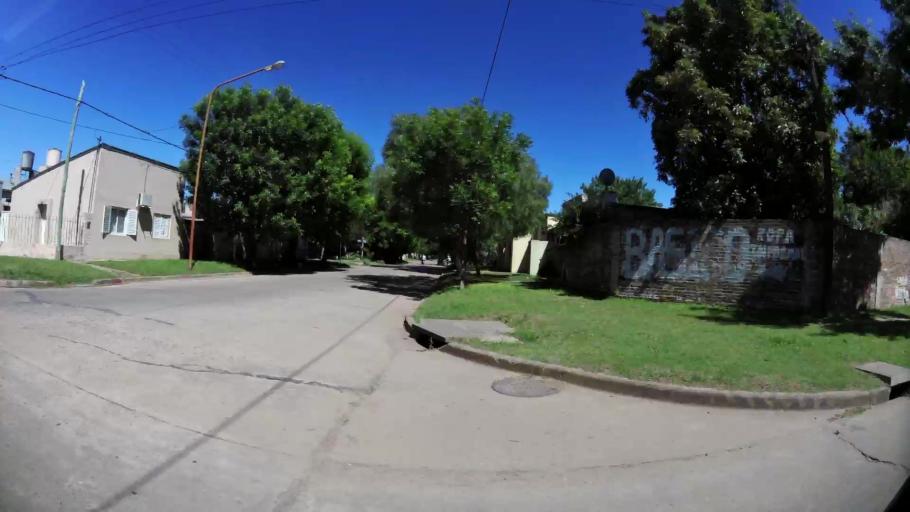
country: AR
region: Santa Fe
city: Esperanza
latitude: -31.4371
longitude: -60.9257
